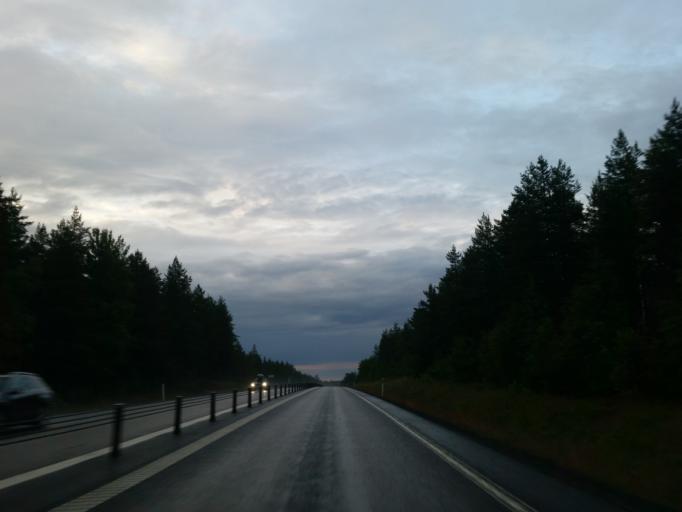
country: SE
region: Vaesterbotten
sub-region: Umea Kommun
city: Saevar
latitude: 63.9382
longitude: 20.6481
